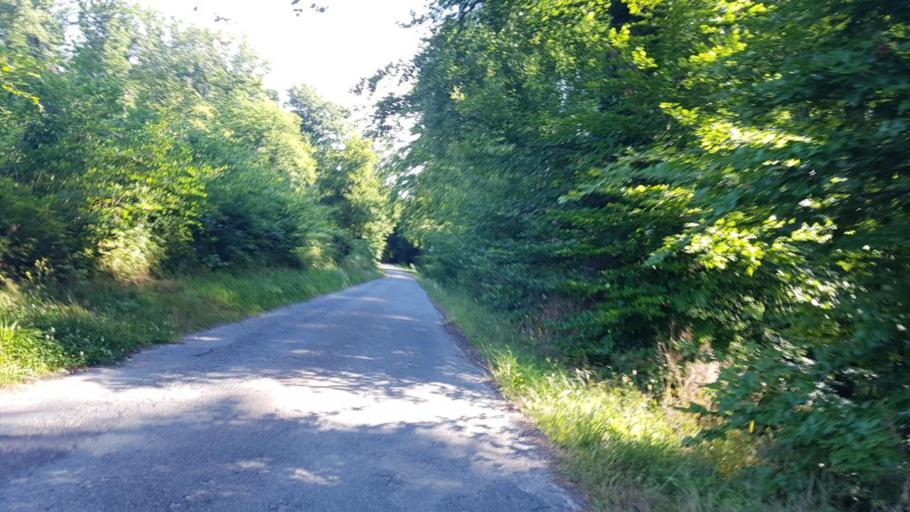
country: FR
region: Picardie
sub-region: Departement de l'Oise
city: Fleurines
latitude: 49.2553
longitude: 2.6188
